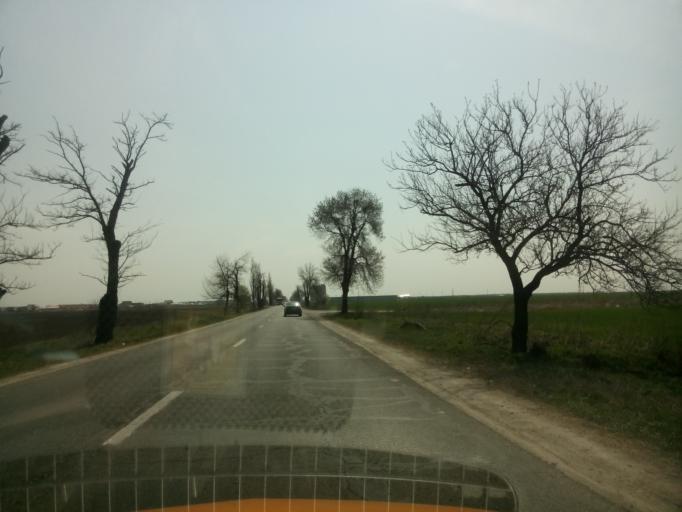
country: RO
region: Ilfov
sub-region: Comuna Glina
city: Glina
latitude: 44.3458
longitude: 26.2252
